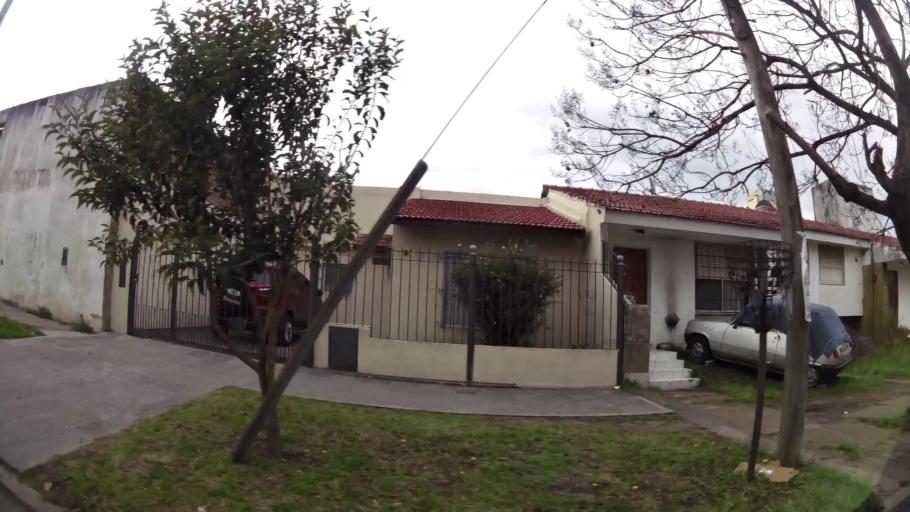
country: AR
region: Buenos Aires
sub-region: Partido de Quilmes
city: Quilmes
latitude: -34.8025
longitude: -58.2728
